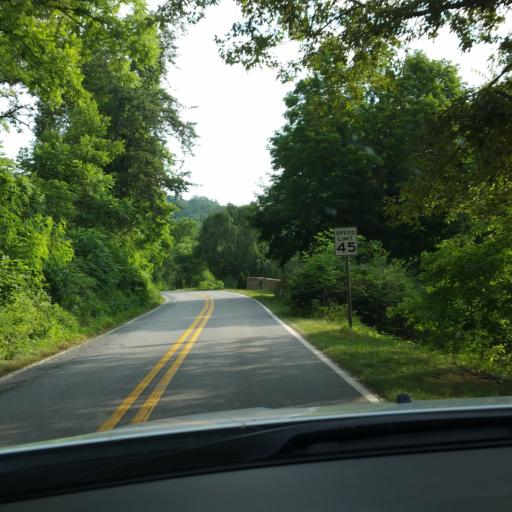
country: US
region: North Carolina
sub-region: Buncombe County
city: Bent Creek
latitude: 35.5180
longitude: -82.6878
